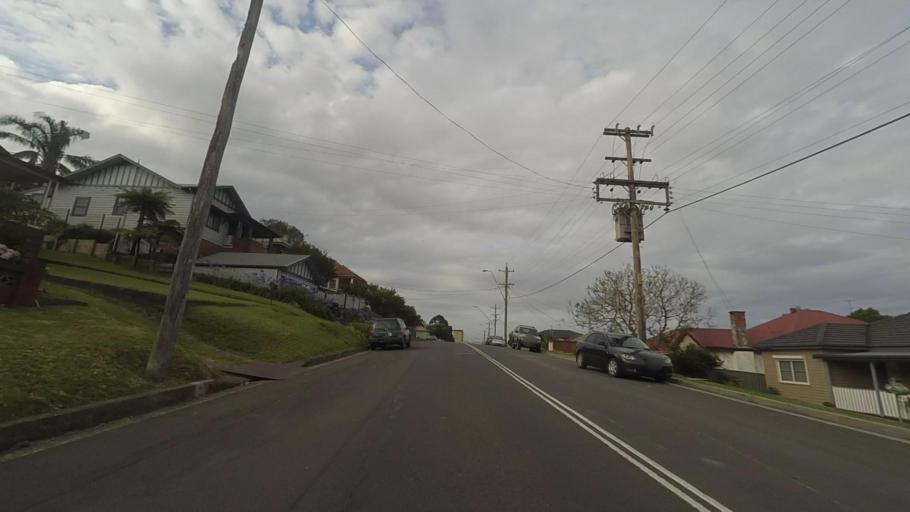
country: AU
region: New South Wales
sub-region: Wollongong
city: Wollongong
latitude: -34.4319
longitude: 150.8861
